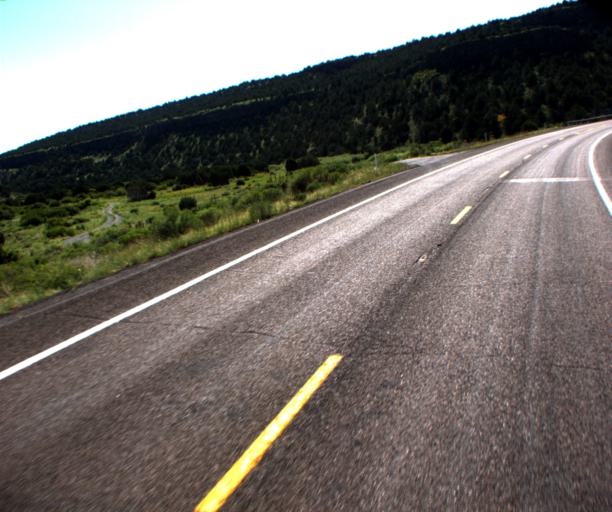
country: US
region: Arizona
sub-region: Apache County
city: Eagar
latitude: 34.0924
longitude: -109.2049
